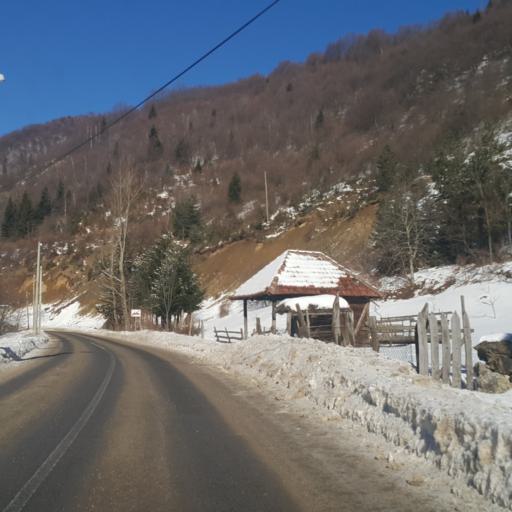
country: XK
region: Mitrovica
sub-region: Komuna e Leposaviqit
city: Leposaviq
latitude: 43.3032
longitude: 20.8803
